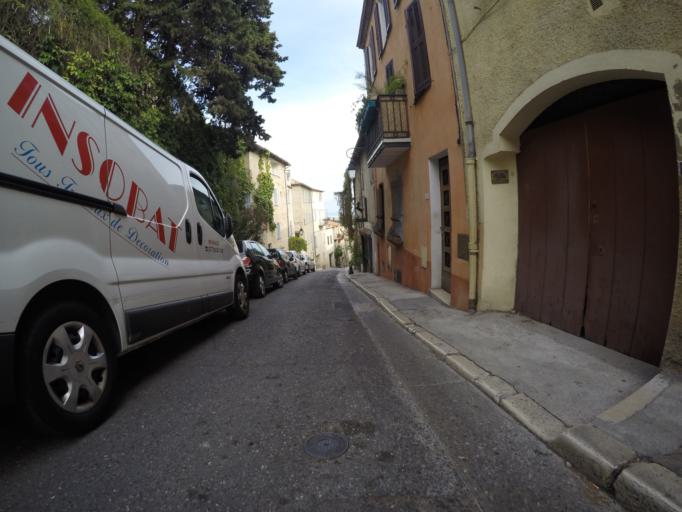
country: FR
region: Provence-Alpes-Cote d'Azur
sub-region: Departement des Alpes-Maritimes
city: Cagnes-sur-Mer
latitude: 43.6652
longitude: 7.1474
